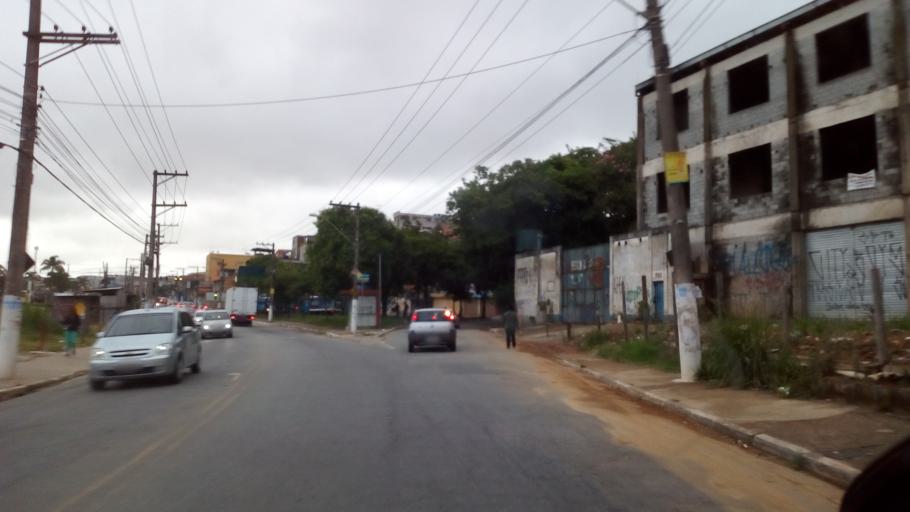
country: BR
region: Sao Paulo
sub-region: Itaquaquecetuba
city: Itaquaquecetuba
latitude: -23.4370
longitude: -46.4068
